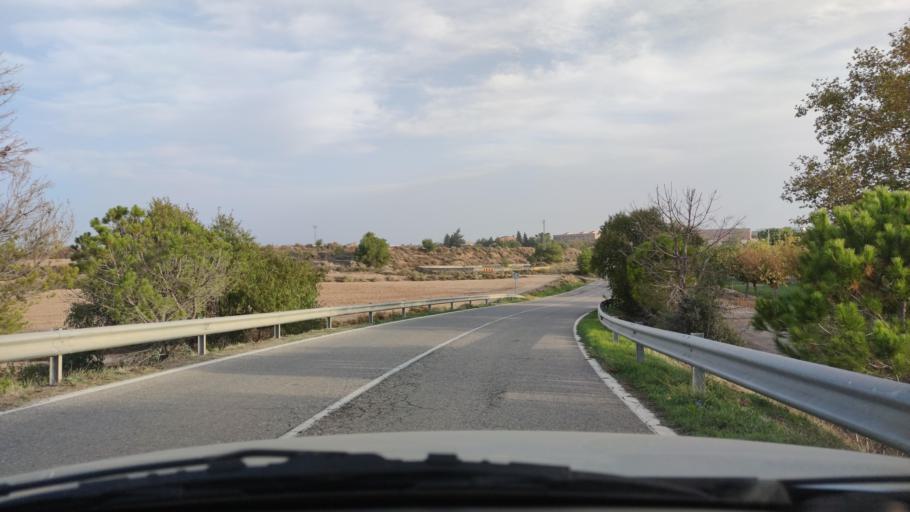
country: ES
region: Catalonia
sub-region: Provincia de Lleida
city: Anglesola
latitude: 41.6465
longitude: 1.0782
